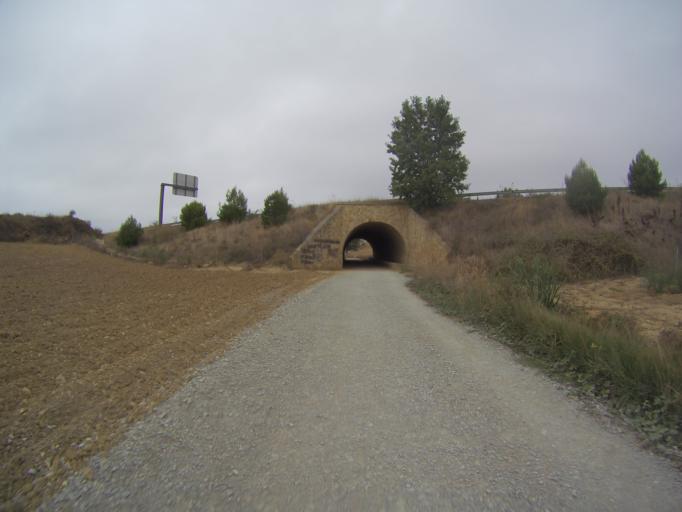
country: ES
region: Navarre
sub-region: Provincia de Navarra
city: Villatuerta
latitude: 42.6634
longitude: -1.9780
